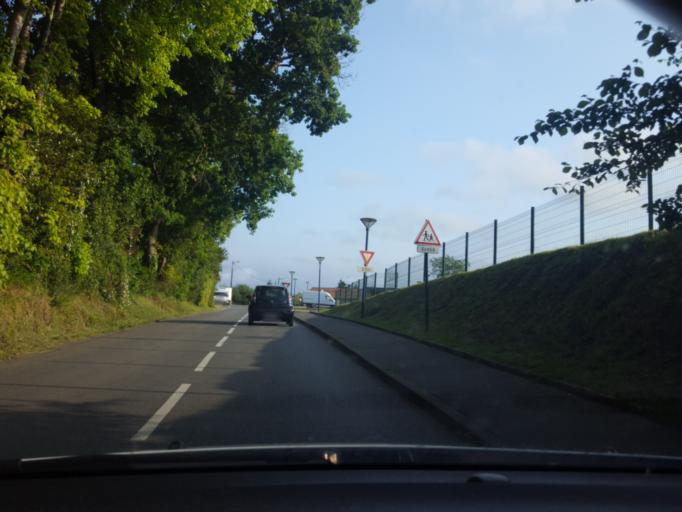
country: FR
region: Aquitaine
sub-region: Departement des Landes
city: Ondres
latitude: 43.5625
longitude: -1.4449
